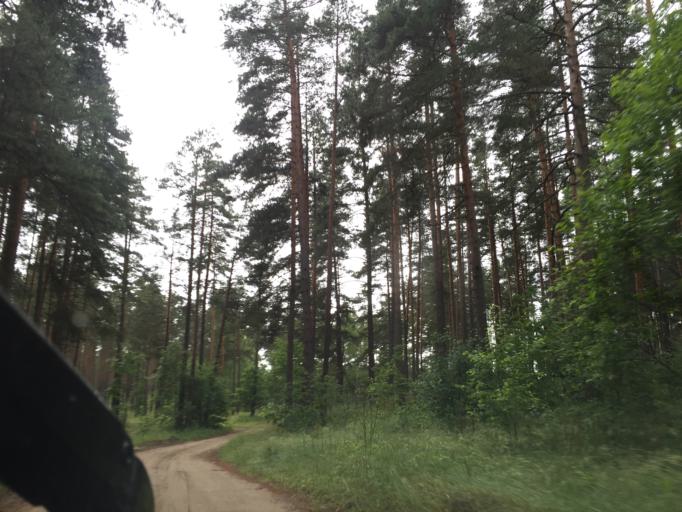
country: LV
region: Riga
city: Jaunciems
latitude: 57.0571
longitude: 24.1846
